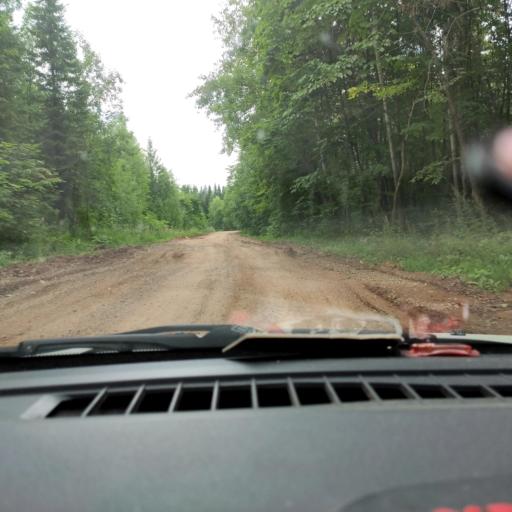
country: RU
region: Perm
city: Kultayevo
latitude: 57.8093
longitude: 56.0038
